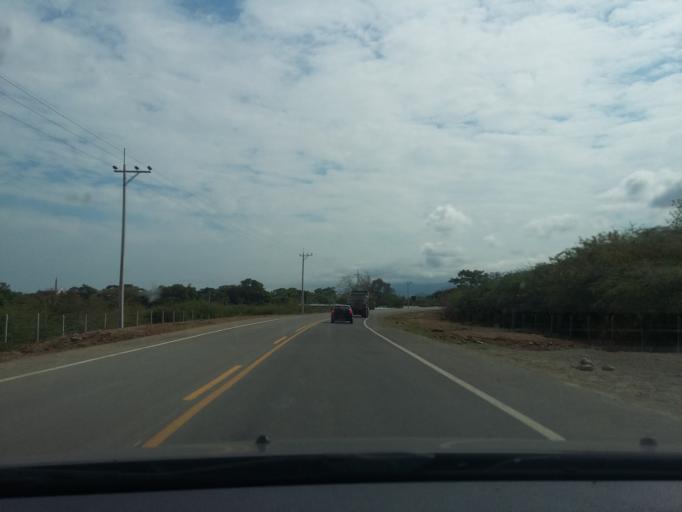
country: CO
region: Tolima
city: Ambalema
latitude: 4.7725
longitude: -74.7647
